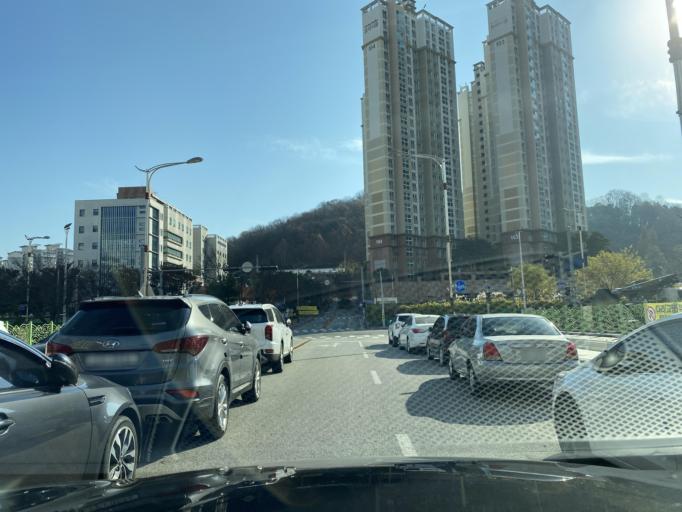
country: KR
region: Chungcheongnam-do
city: Cheonan
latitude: 36.8001
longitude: 127.1078
